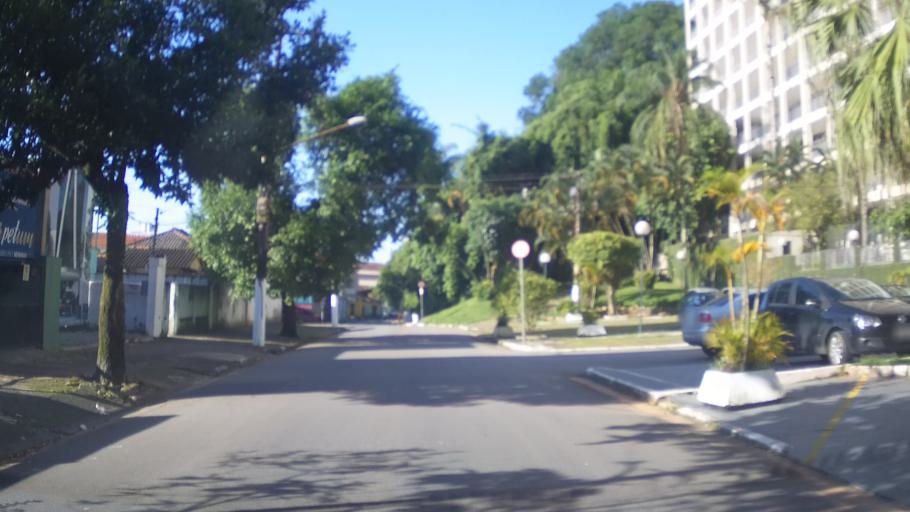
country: BR
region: Sao Paulo
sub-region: Santos
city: Santos
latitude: -23.9481
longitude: -46.3432
